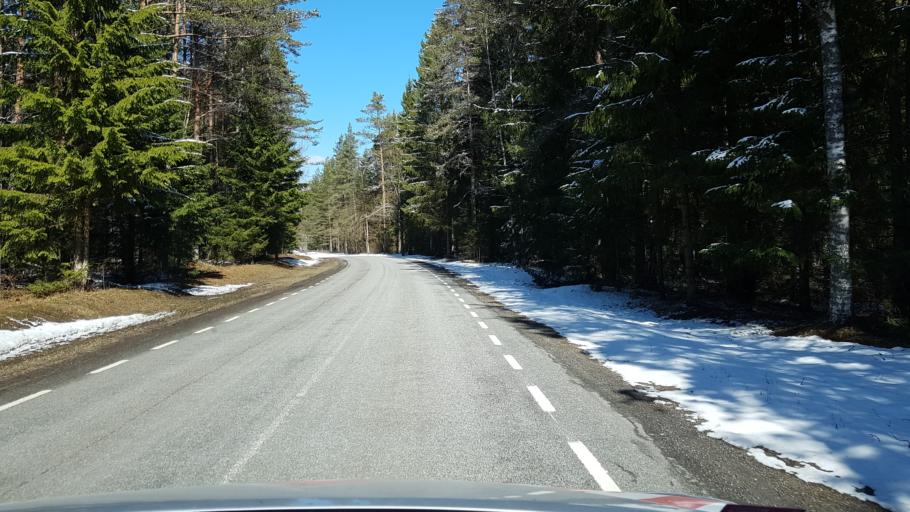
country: EE
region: Laeaene-Virumaa
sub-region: Kadrina vald
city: Kadrina
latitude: 59.4542
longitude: 26.0140
